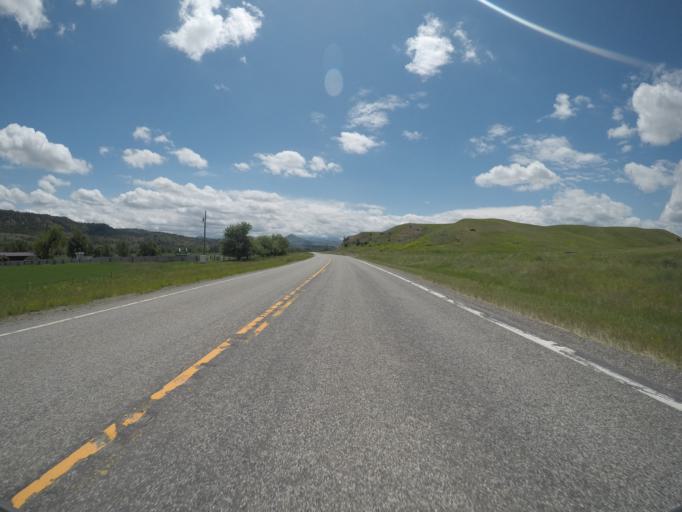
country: US
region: Montana
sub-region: Sweet Grass County
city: Big Timber
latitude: 45.7521
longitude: -109.9936
